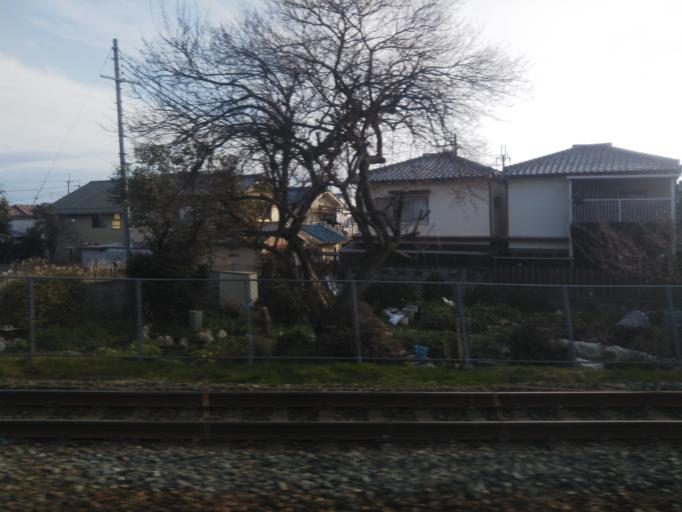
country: JP
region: Shiga Prefecture
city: Otsu-shi
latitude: 34.9894
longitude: 135.8888
